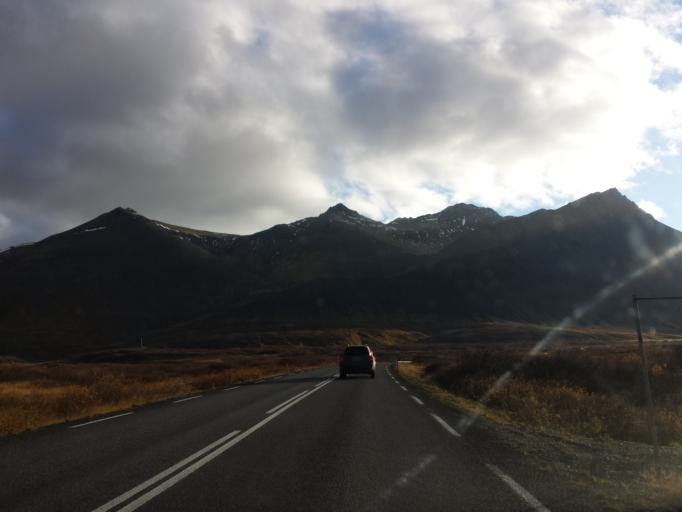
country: IS
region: West
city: Borgarnes
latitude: 64.5206
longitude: -21.8866
